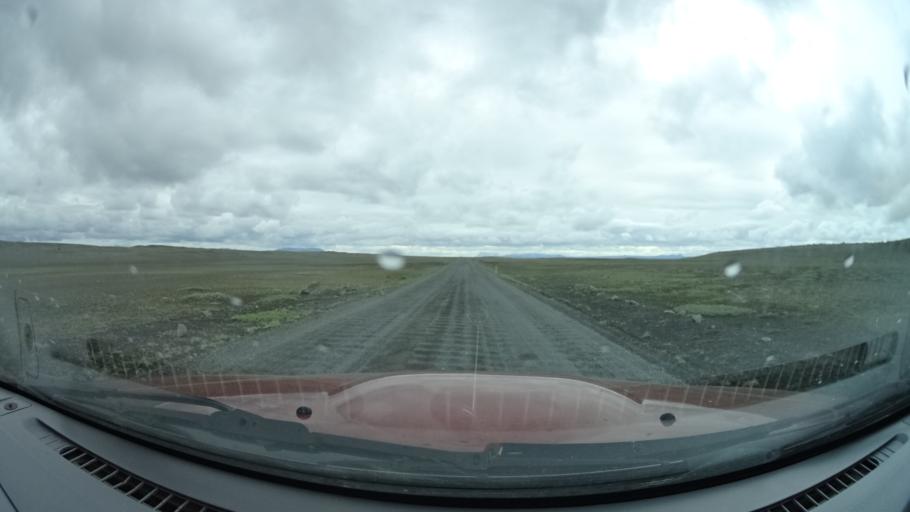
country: IS
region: Northeast
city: Laugar
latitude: 65.7149
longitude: -16.3281
